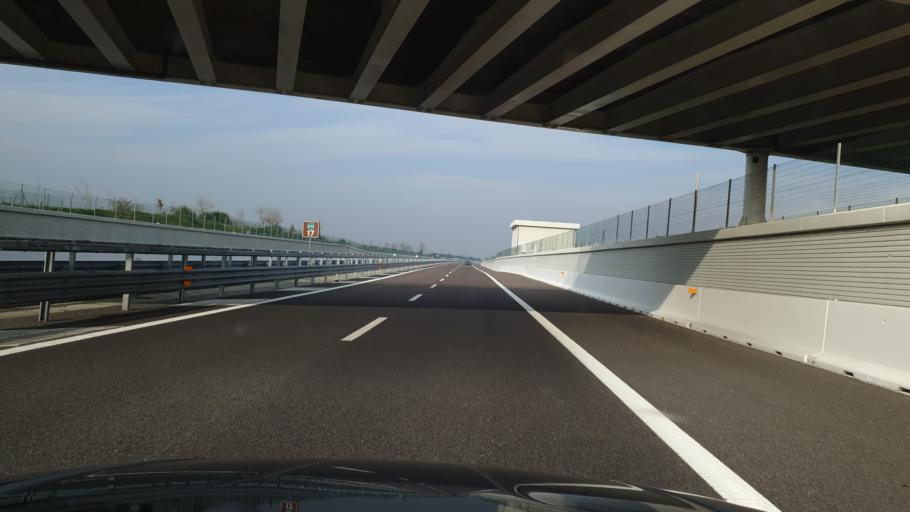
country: IT
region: Veneto
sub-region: Provincia di Vicenza
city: Agugliaro
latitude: 45.3156
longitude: 11.5772
